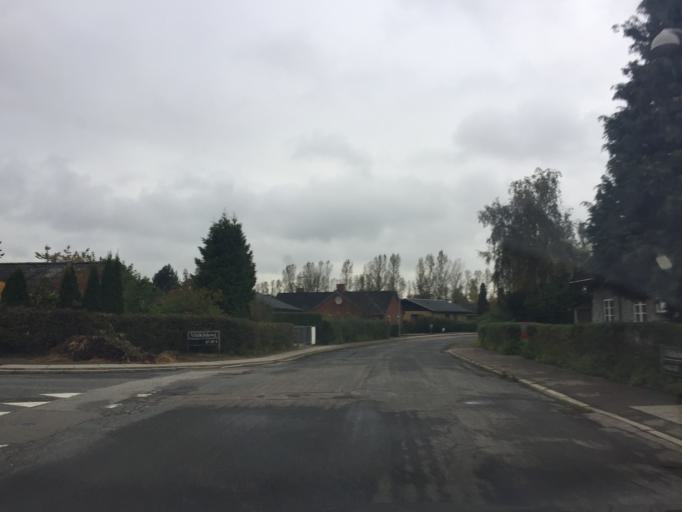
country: DK
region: Capital Region
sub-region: Hoje-Taastrup Kommune
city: Flong
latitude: 55.6536
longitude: 12.2027
